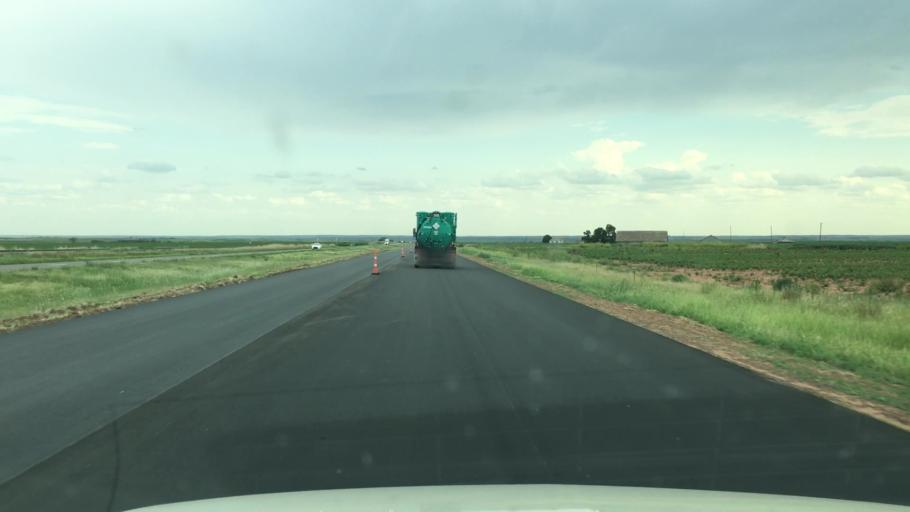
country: US
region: Texas
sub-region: Hall County
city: Memphis
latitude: 34.6221
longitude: -100.4729
